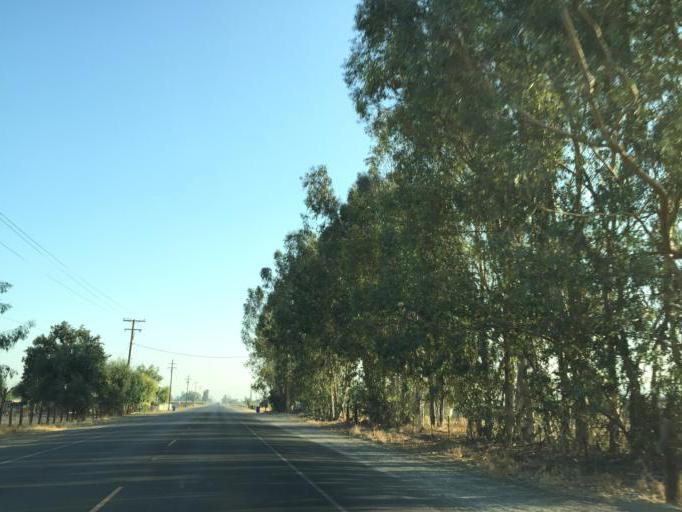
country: US
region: California
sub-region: Tulare County
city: Cutler
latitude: 36.4432
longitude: -119.2956
